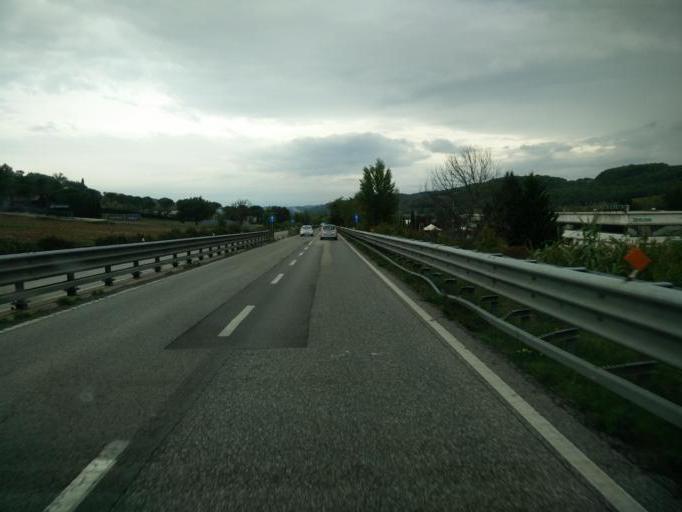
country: IT
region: Tuscany
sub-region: Province of Florence
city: Sambuca
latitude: 43.5837
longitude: 11.2026
